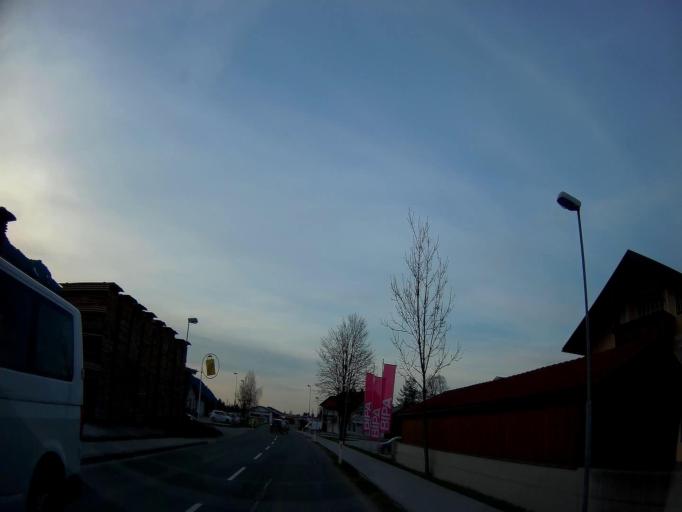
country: AT
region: Salzburg
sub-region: Politischer Bezirk Hallein
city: Kuchl
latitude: 47.6309
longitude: 13.1419
